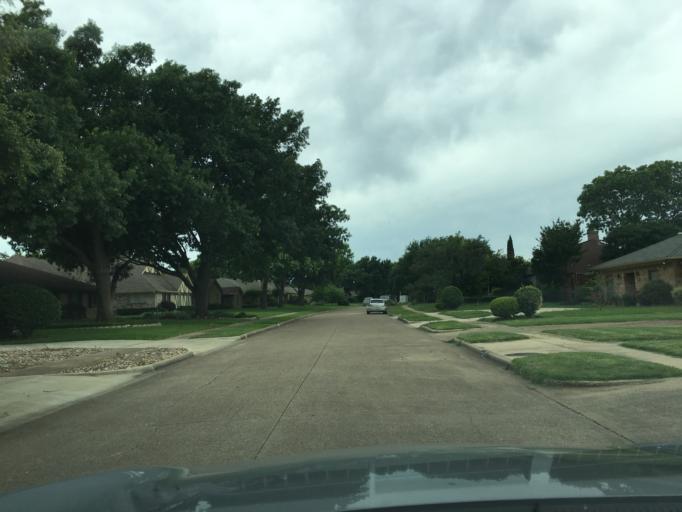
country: US
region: Texas
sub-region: Dallas County
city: Richardson
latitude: 32.9406
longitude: -96.7099
